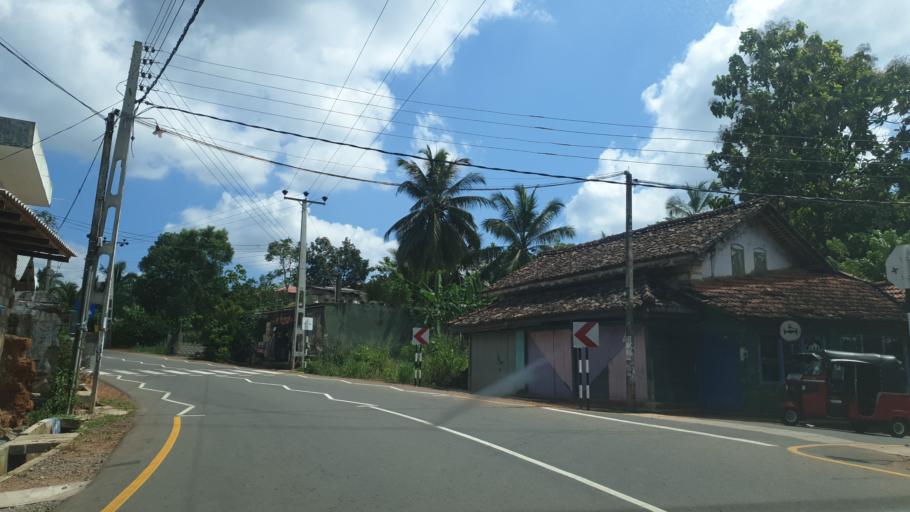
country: LK
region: Western
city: Panadura
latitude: 6.6654
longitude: 79.9591
